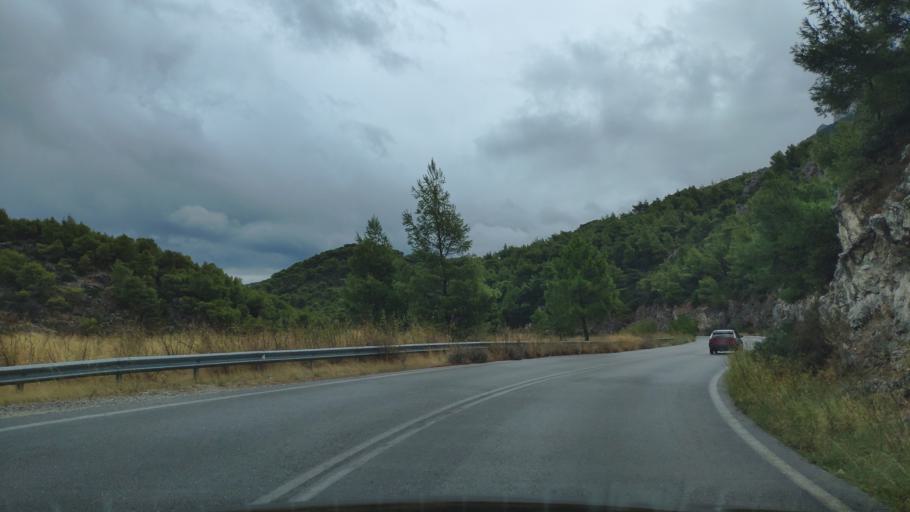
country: GR
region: Peloponnese
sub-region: Nomos Korinthias
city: Perachora
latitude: 38.0095
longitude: 22.9424
